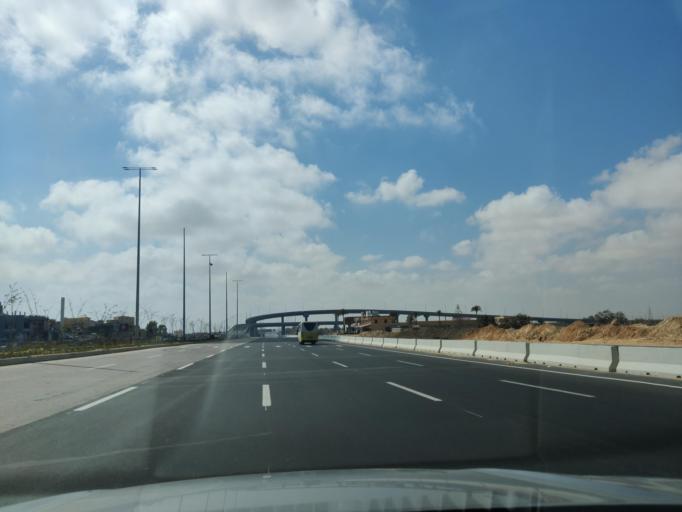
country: EG
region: Muhafazat Matruh
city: Al `Alamayn
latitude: 30.9549
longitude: 28.7676
